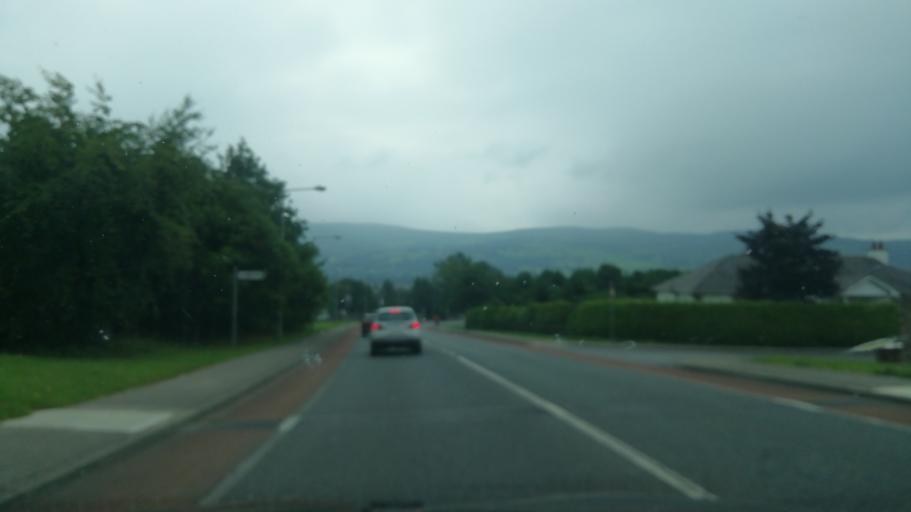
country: IE
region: Munster
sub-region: South Tipperary
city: Cluain Meala
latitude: 52.3675
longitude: -7.7003
